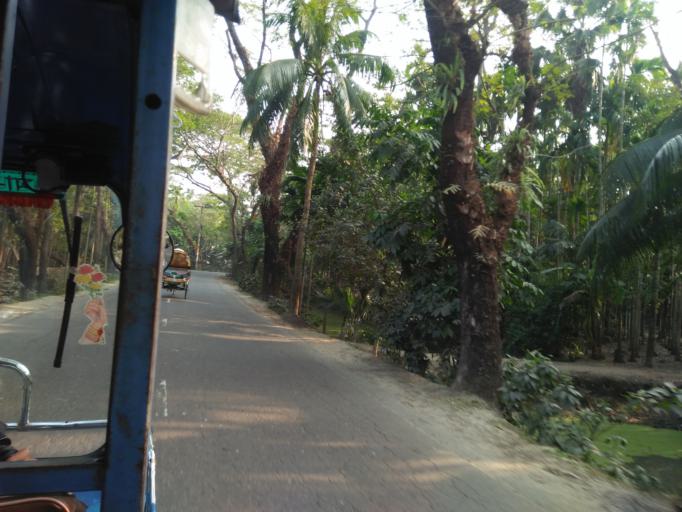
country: BD
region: Barisal
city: Bhola
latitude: 22.7042
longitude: 90.6409
